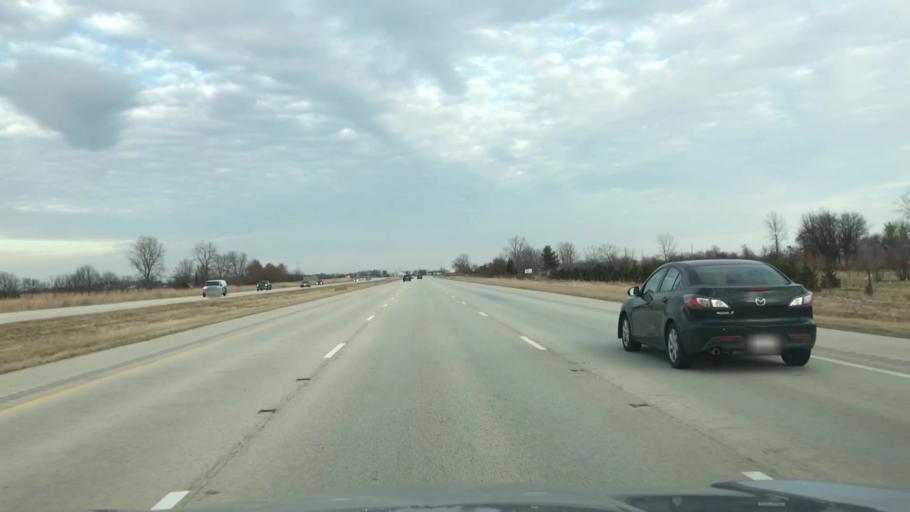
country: US
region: Illinois
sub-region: Sangamon County
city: Williamsville
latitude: 39.9661
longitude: -89.5426
